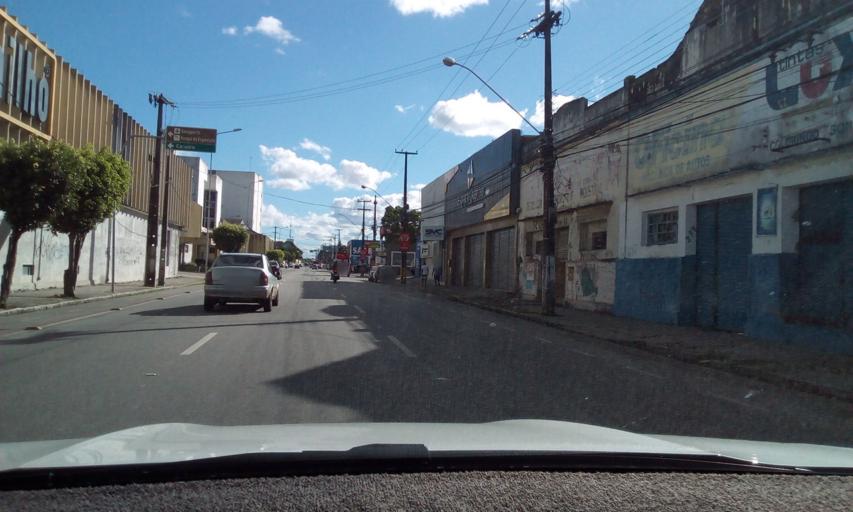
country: BR
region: Paraiba
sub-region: Campina Grande
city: Campina Grande
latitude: -7.2278
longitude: -35.8876
